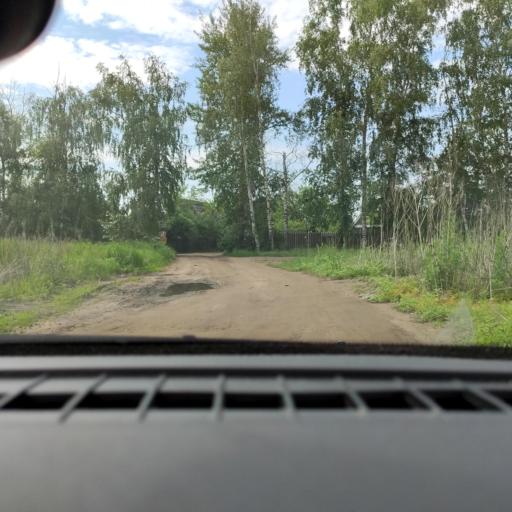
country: RU
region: Voronezj
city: Maslovka
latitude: 51.5058
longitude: 39.2007
